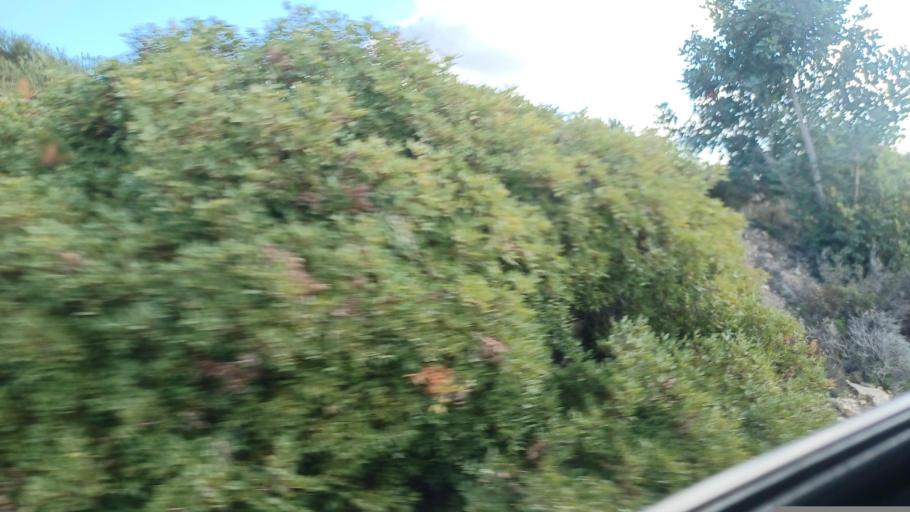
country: CY
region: Limassol
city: Pano Polemidia
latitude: 34.7697
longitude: 32.9794
